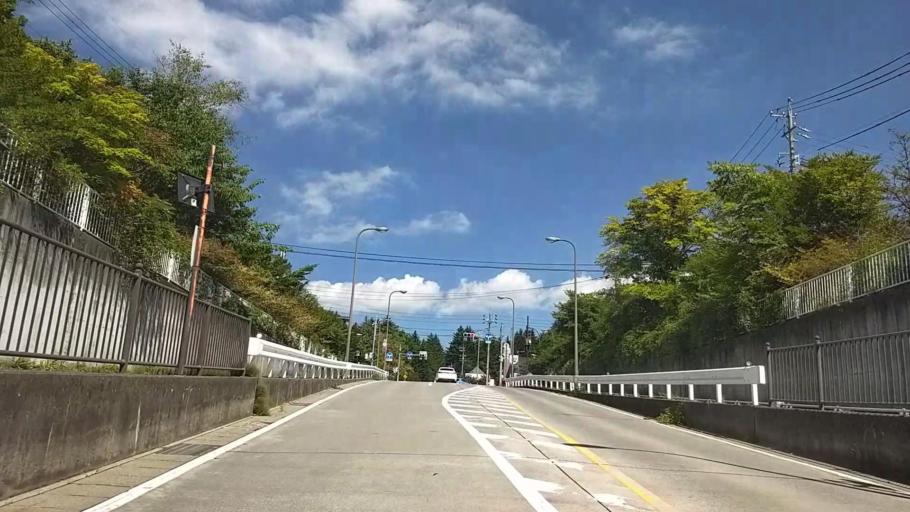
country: JP
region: Nagano
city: Saku
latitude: 36.3435
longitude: 138.6303
